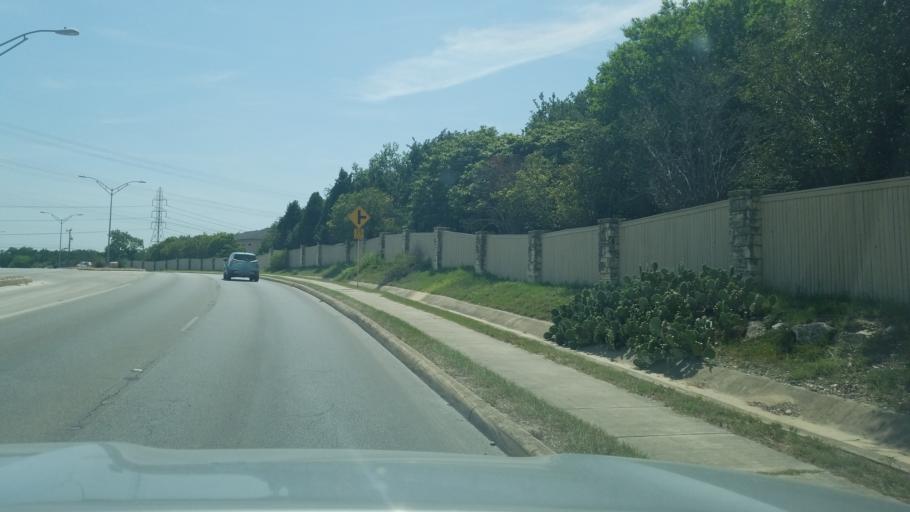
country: US
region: Texas
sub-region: Bexar County
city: Hollywood Park
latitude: 29.6198
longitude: -98.5155
